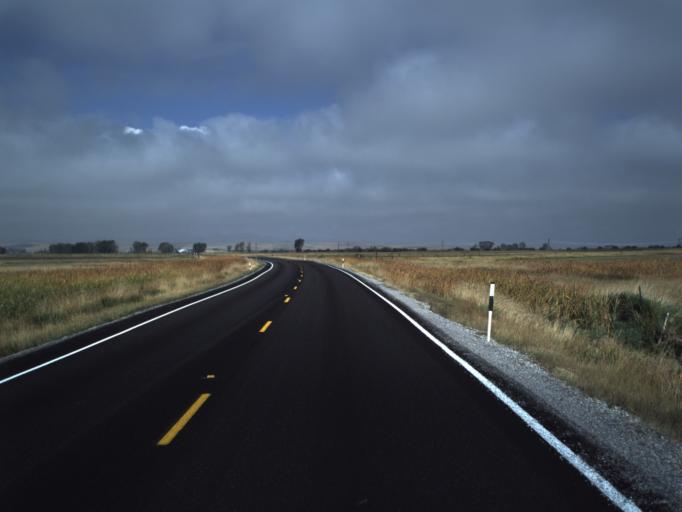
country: US
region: Utah
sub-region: Rich County
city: Randolph
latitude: 41.5090
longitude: -111.1289
